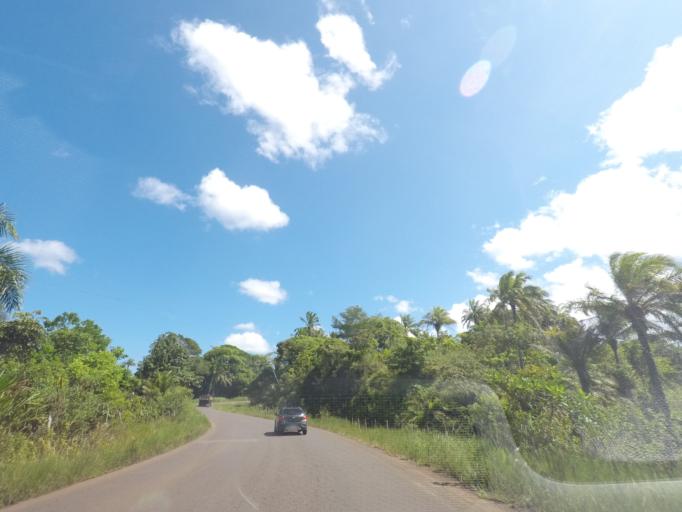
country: BR
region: Bahia
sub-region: Taperoa
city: Taperoa
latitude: -13.5852
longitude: -39.1062
